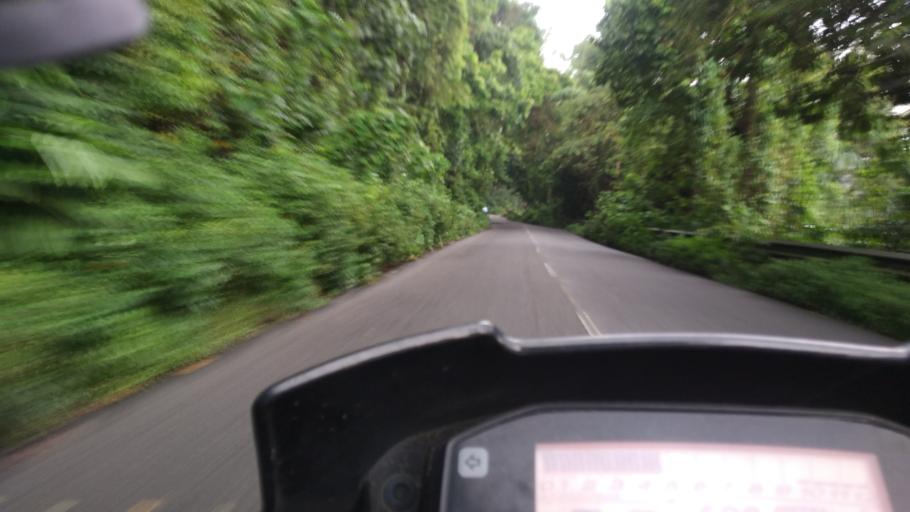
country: IN
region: Kerala
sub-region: Idukki
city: Kuttampuzha
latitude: 10.0653
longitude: 76.7832
